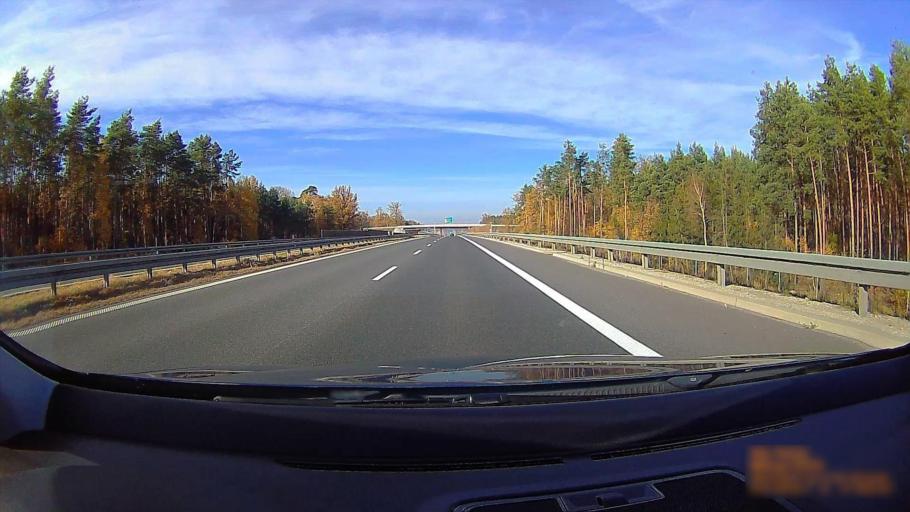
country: PL
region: Greater Poland Voivodeship
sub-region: Powiat ostrowski
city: Ostrow Wielkopolski
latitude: 51.6531
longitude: 17.8681
